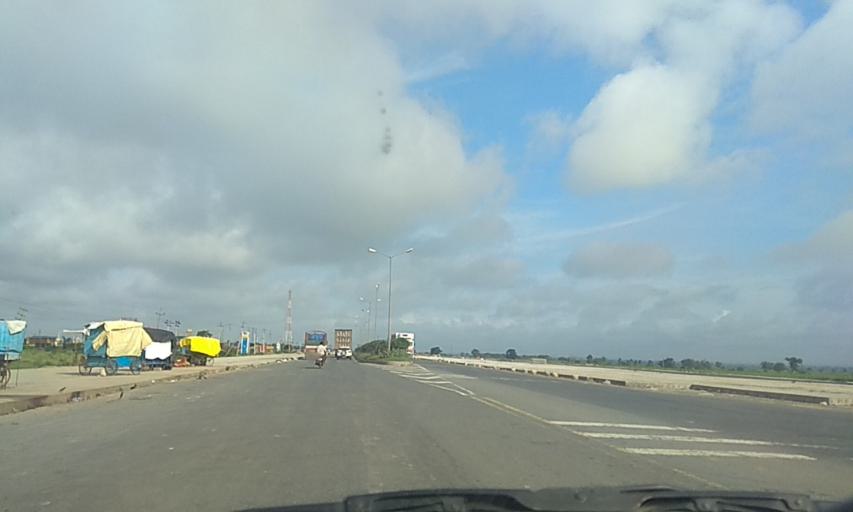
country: IN
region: Karnataka
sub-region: Haveri
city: Savanur
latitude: 14.9106
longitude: 75.2791
